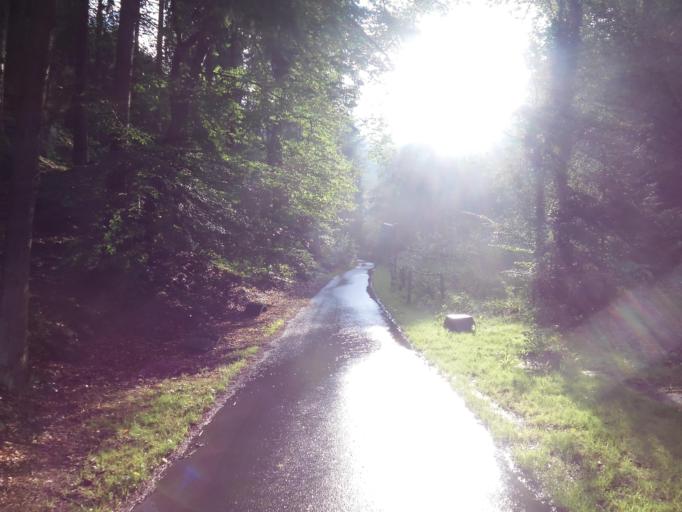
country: CZ
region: Central Bohemia
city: Mseno
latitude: 50.4356
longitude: 14.5837
